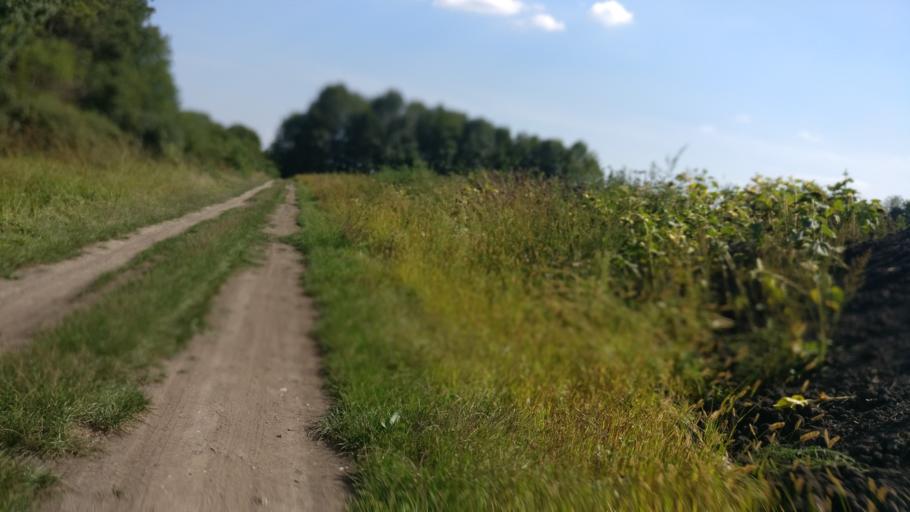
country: AT
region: Lower Austria
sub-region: Politischer Bezirk Baden
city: Ebreichsdorf
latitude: 47.9902
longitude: 16.4033
